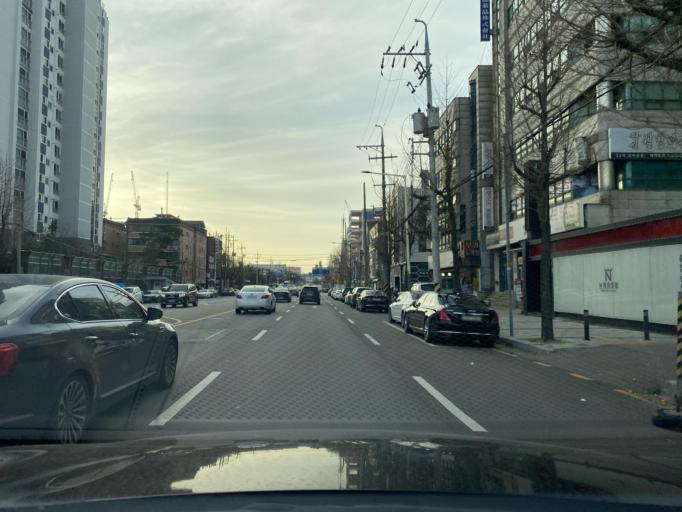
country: KR
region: Incheon
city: Incheon
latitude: 37.5065
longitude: 126.6702
